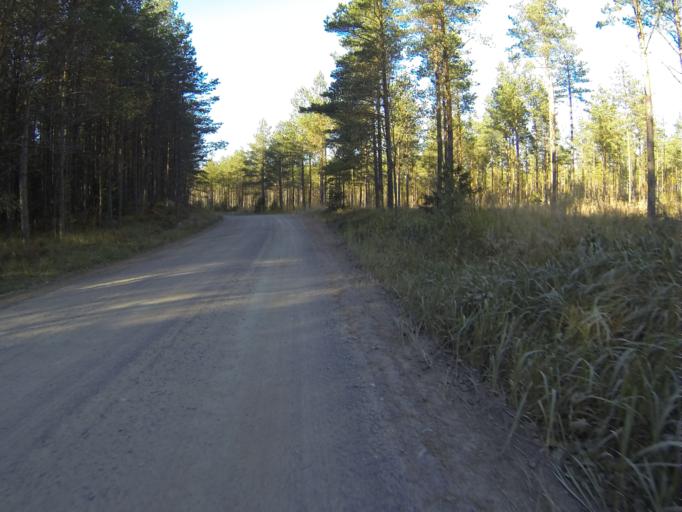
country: FI
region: Varsinais-Suomi
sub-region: Salo
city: Saerkisalo
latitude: 60.2265
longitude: 22.9825
